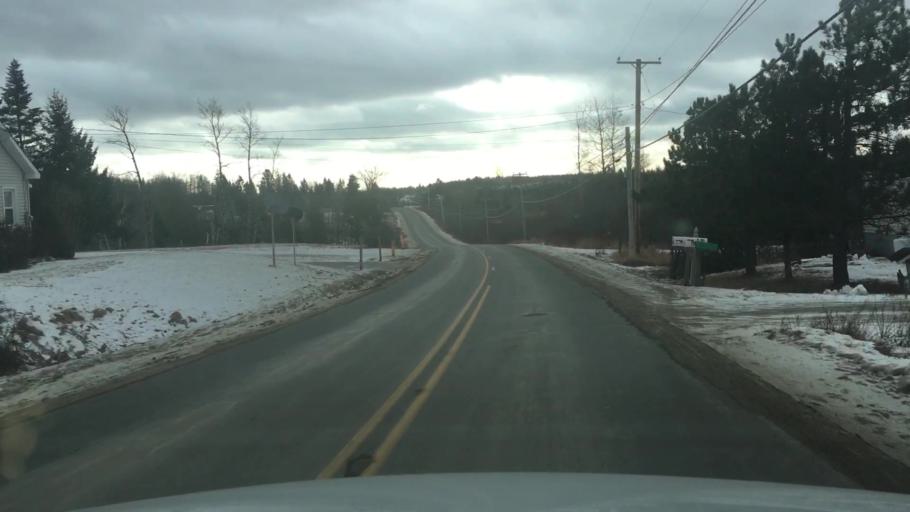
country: US
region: Maine
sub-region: Washington County
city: Machias
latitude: 44.6843
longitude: -67.4668
